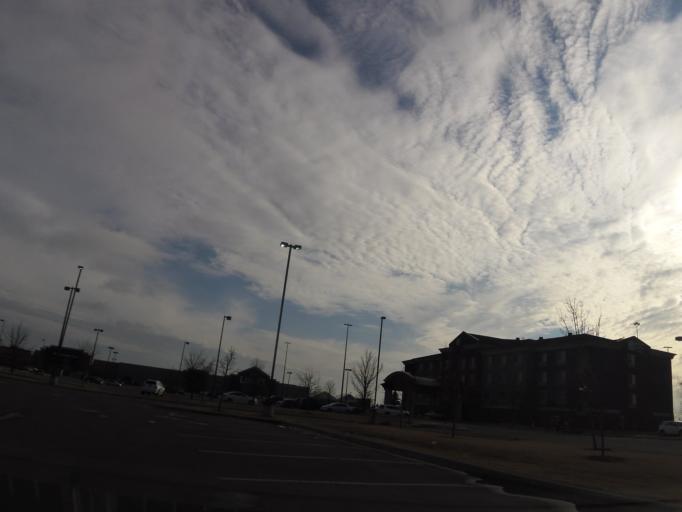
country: US
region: North Dakota
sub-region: Grand Forks County
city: Grand Forks
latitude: 47.8888
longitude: -97.0848
